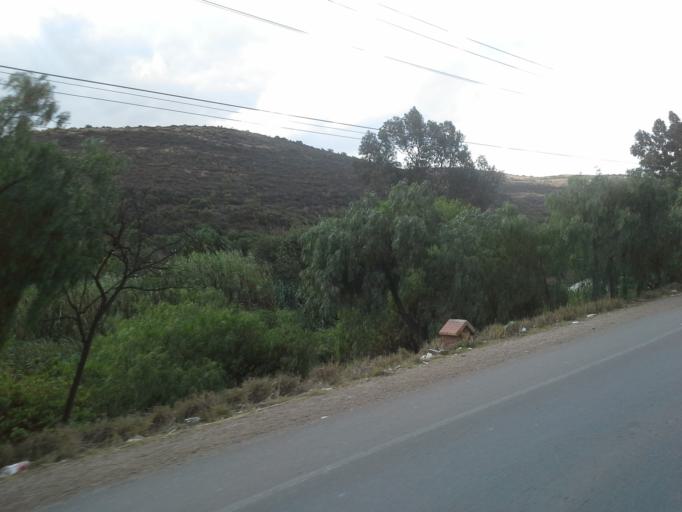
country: BO
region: Cochabamba
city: Tarata
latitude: -17.5155
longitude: -66.0876
